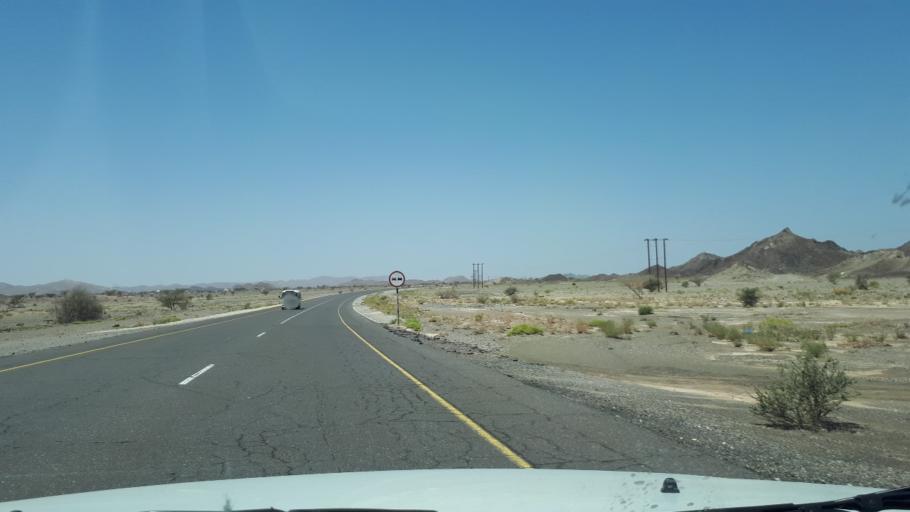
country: OM
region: Ash Sharqiyah
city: Ibra'
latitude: 22.6198
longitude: 58.4432
